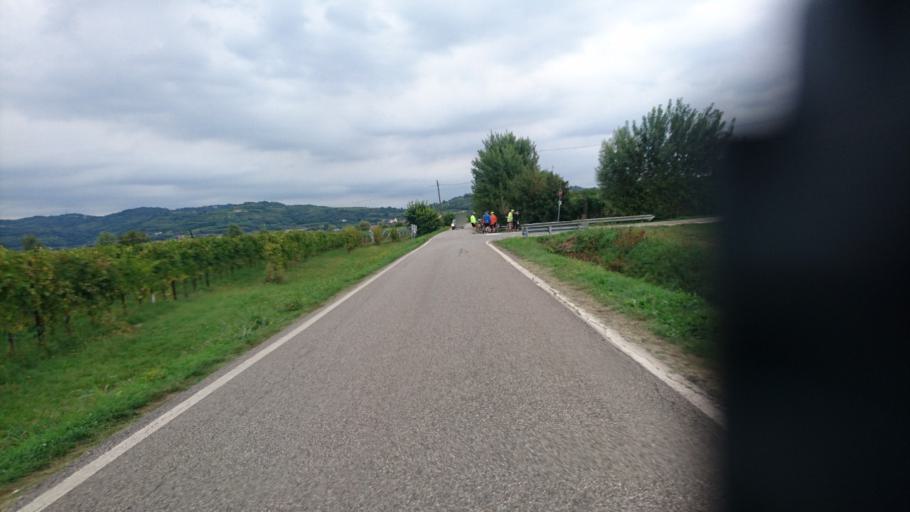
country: IT
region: Veneto
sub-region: Provincia di Vicenza
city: Gambellara
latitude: 45.4391
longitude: 11.3379
